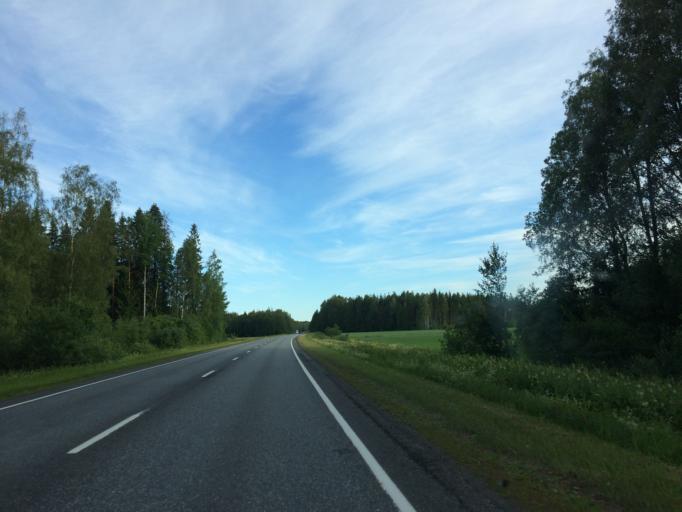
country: FI
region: Haeme
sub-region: Haemeenlinna
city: Janakkala
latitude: 60.9235
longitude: 24.5375
